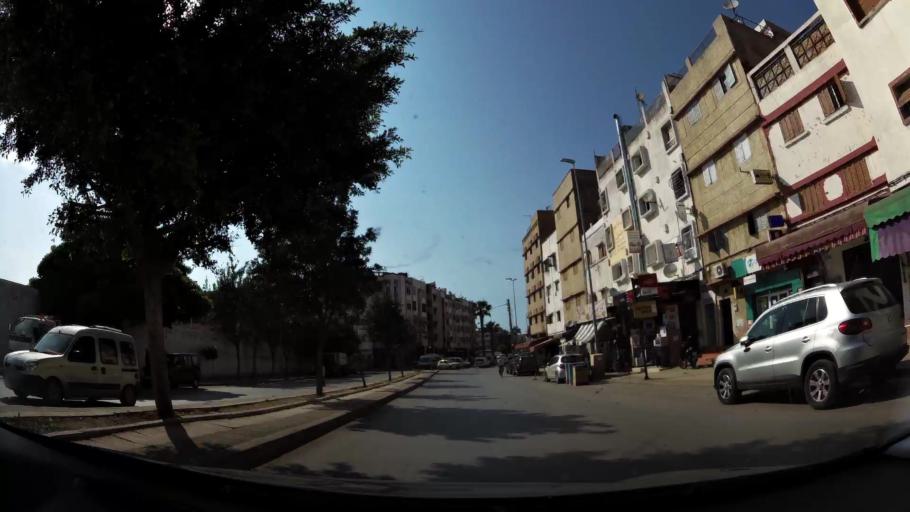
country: MA
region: Rabat-Sale-Zemmour-Zaer
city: Sale
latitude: 34.0522
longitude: -6.7916
